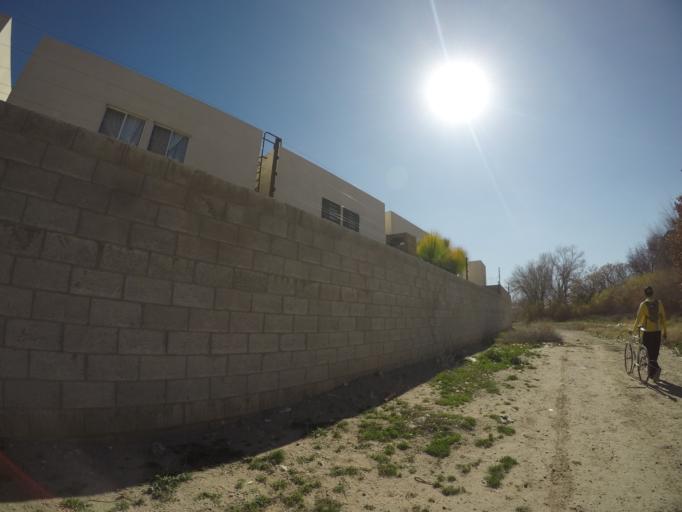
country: US
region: Texas
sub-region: El Paso County
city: Socorro
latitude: 31.6638
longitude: -106.3768
